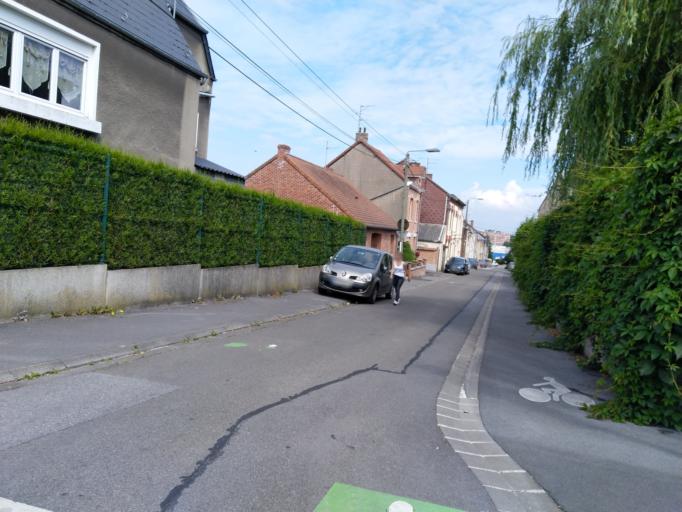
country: FR
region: Nord-Pas-de-Calais
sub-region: Departement du Nord
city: Maubeuge
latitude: 50.2693
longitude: 3.9745
